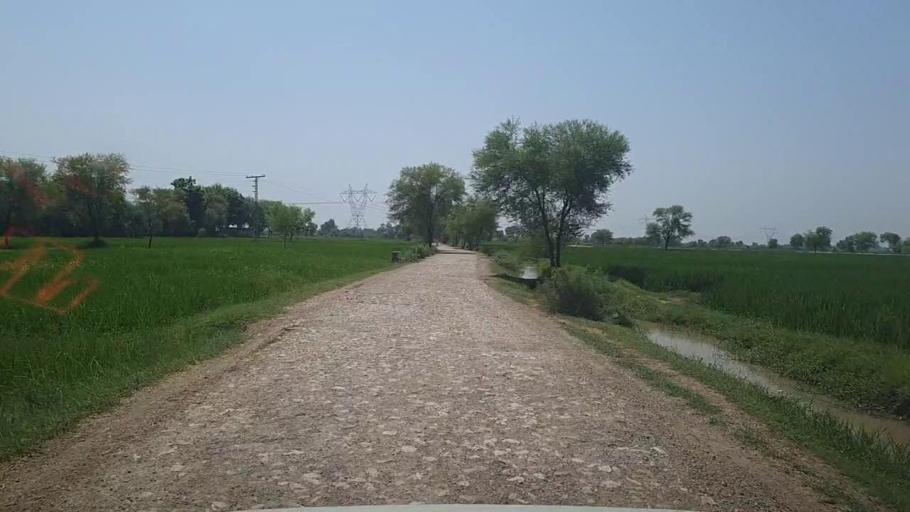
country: PK
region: Sindh
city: Kandhkot
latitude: 28.3169
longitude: 69.3629
